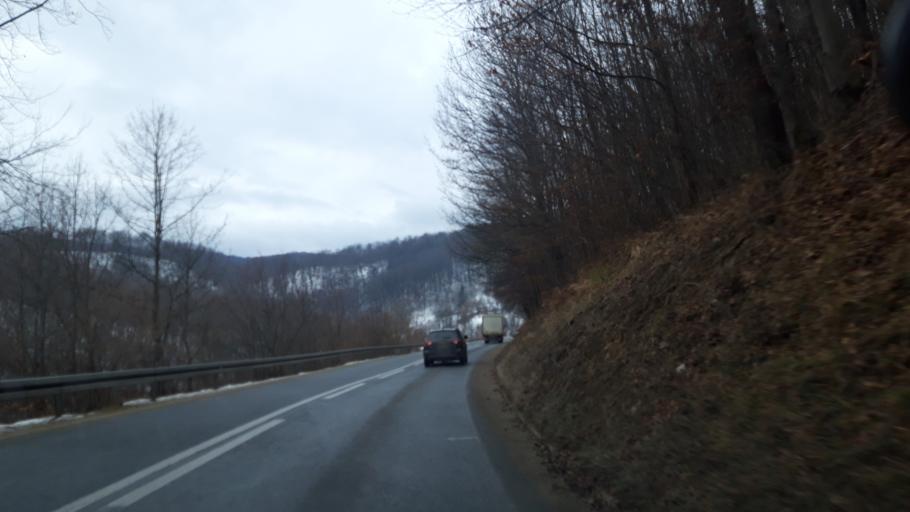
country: BA
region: Republika Srpska
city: Vlasenica
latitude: 44.1812
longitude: 18.9822
